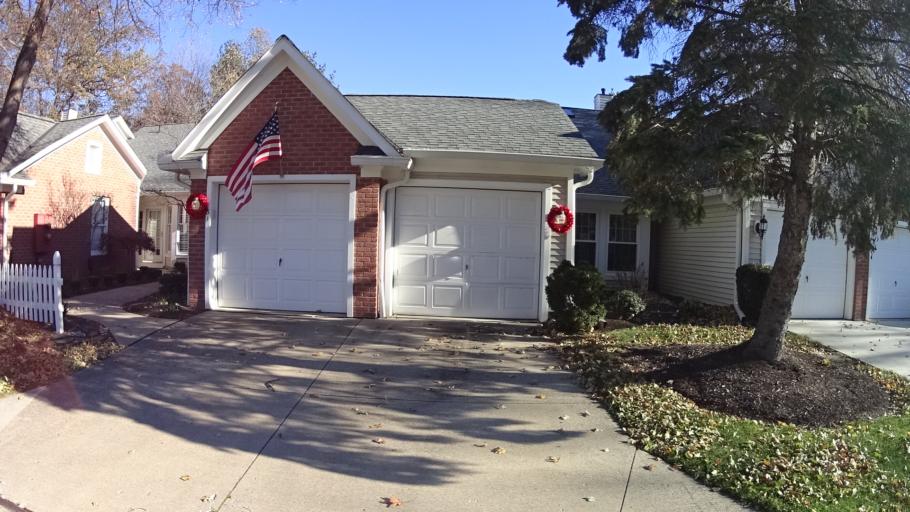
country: US
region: Ohio
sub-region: Lorain County
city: Avon Lake
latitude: 41.5009
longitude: -81.9788
